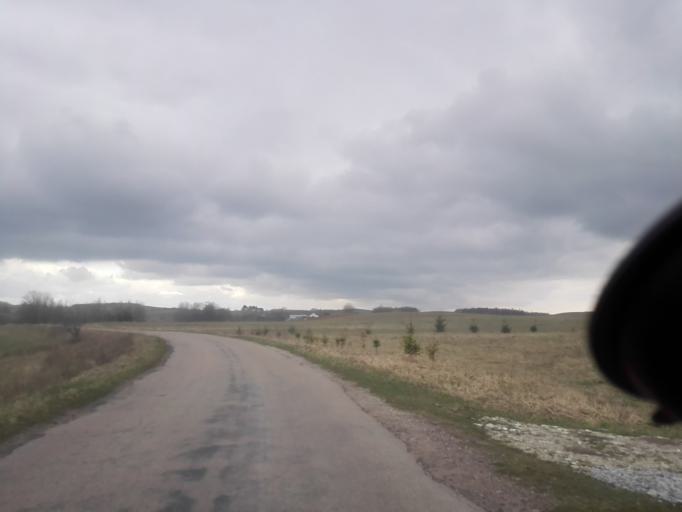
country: PL
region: Podlasie
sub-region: Suwalki
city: Suwalki
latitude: 54.2412
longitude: 22.9762
